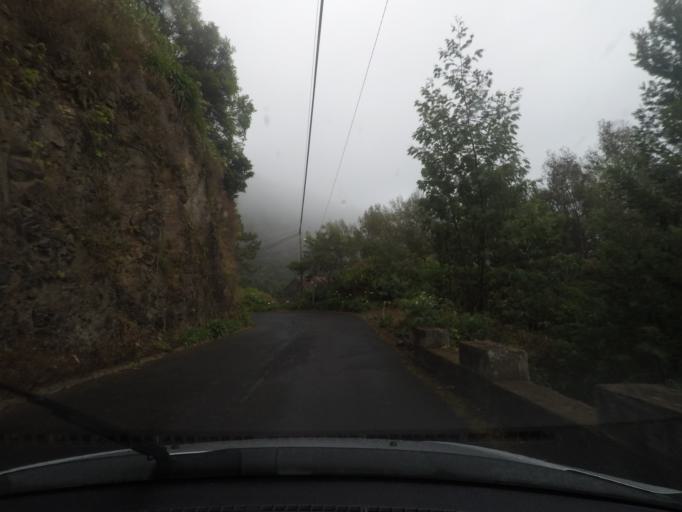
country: PT
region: Madeira
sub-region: Santana
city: Santana
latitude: 32.7815
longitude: -16.8615
